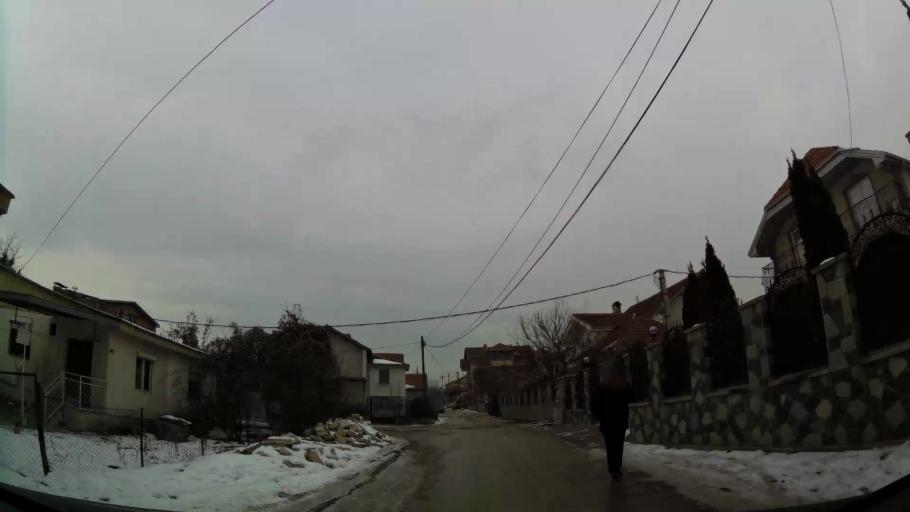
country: MK
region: Suto Orizari
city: Suto Orizare
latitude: 42.0327
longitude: 21.4260
